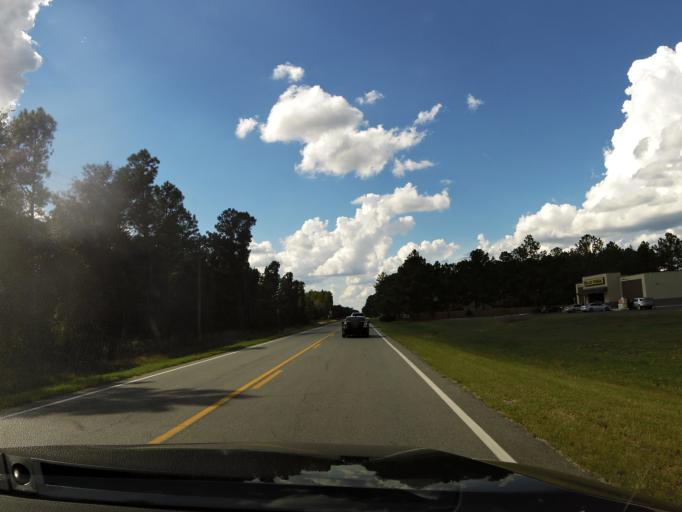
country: US
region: Georgia
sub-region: Echols County
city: Statenville
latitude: 30.7724
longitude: -83.1427
